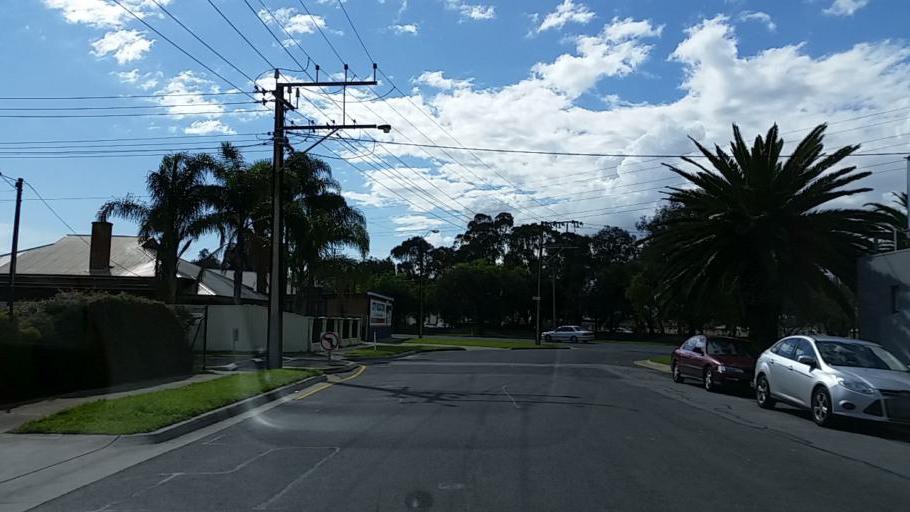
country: AU
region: South Australia
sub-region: Charles Sturt
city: Albert Park
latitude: -34.8740
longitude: 138.5236
